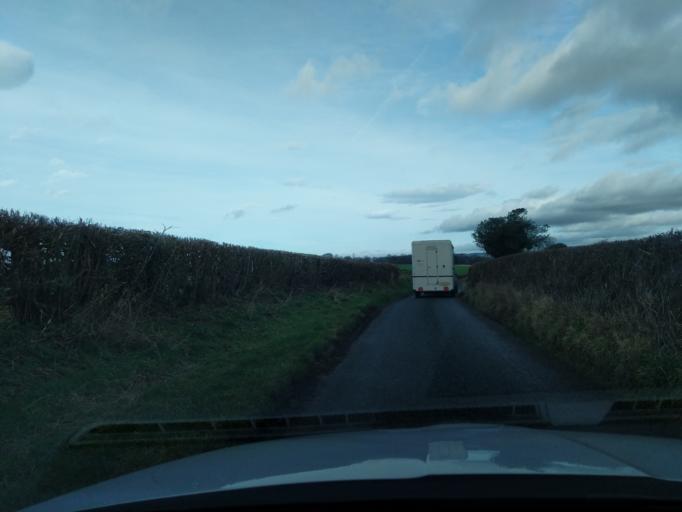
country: GB
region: England
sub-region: North Yorkshire
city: Catterick
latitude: 54.3640
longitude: -1.6656
